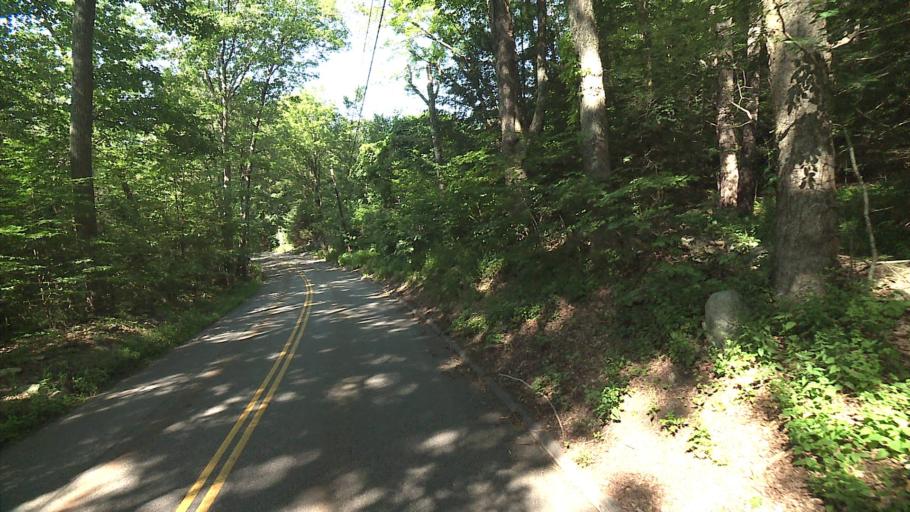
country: US
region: Connecticut
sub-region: Litchfield County
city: Winchester Center
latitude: 41.9013
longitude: -73.1712
